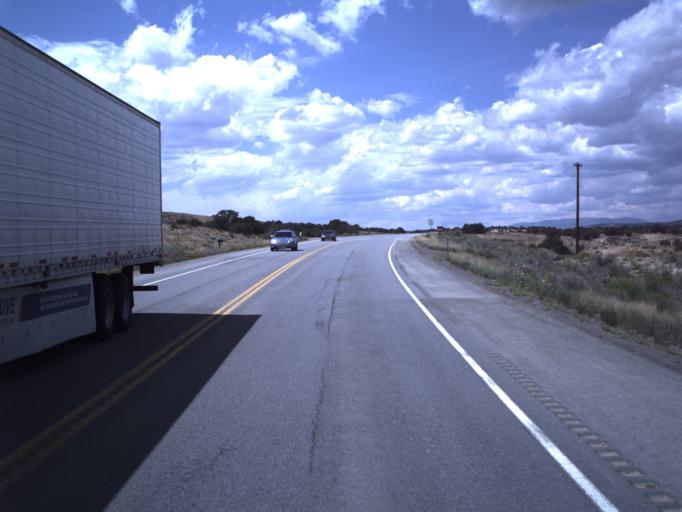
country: US
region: Utah
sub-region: Duchesne County
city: Duchesne
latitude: 40.1751
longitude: -110.5047
